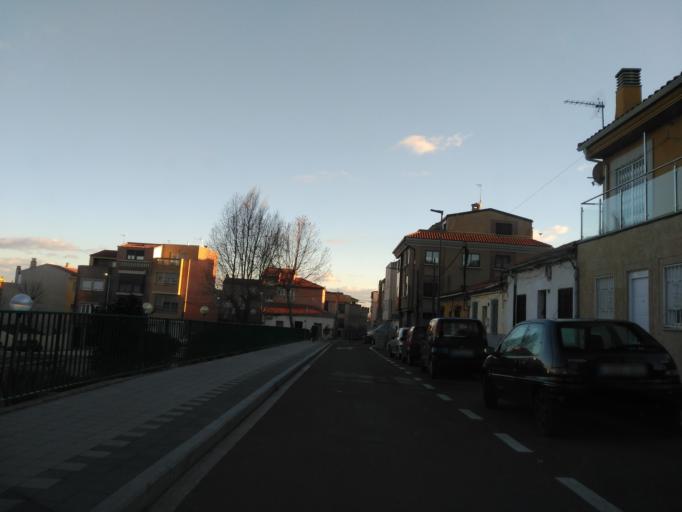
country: ES
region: Castille and Leon
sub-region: Provincia de Salamanca
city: Salamanca
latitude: 40.9782
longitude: -5.6778
